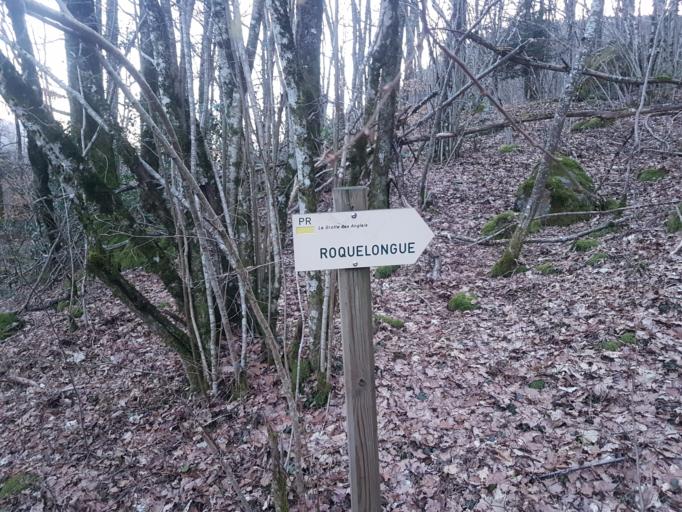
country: FR
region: Auvergne
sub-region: Departement du Cantal
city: Vic-sur-Cere
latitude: 44.9914
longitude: 2.6312
